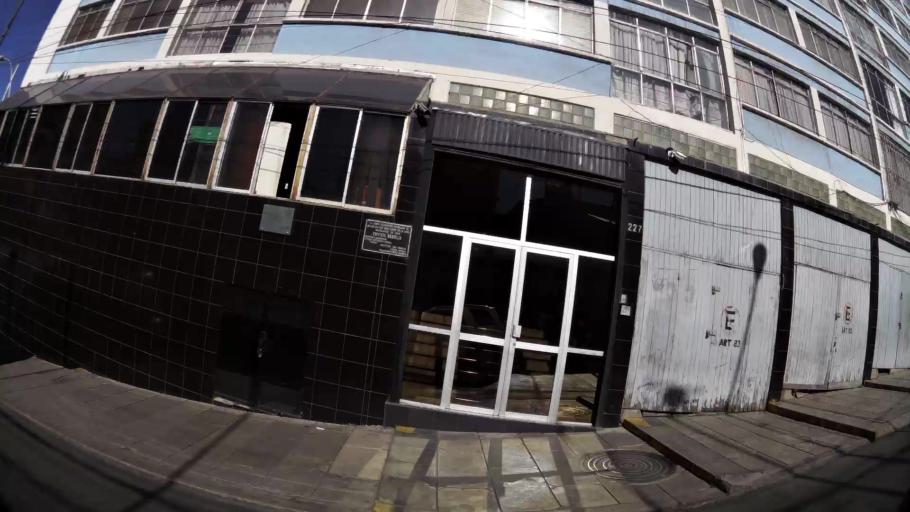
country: BO
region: La Paz
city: La Paz
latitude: -16.5055
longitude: -68.1300
